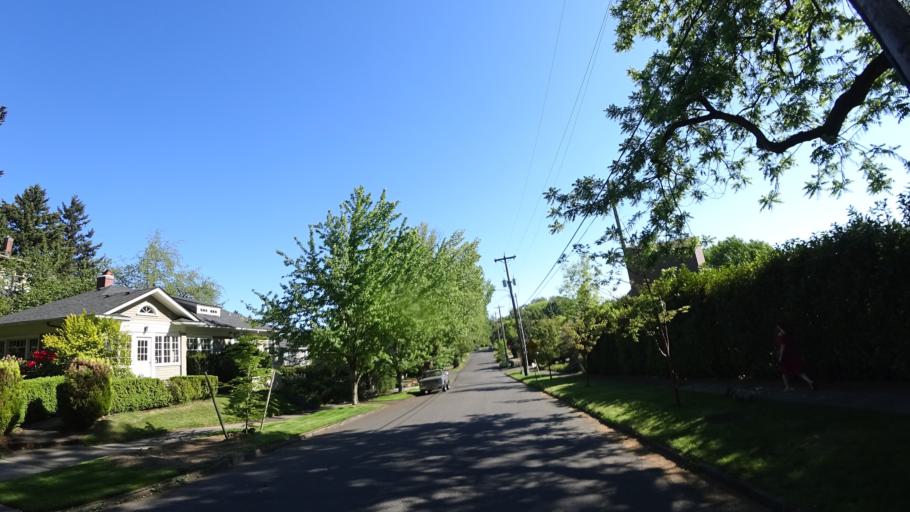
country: US
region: Oregon
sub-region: Multnomah County
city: Portland
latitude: 45.5300
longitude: -122.6307
